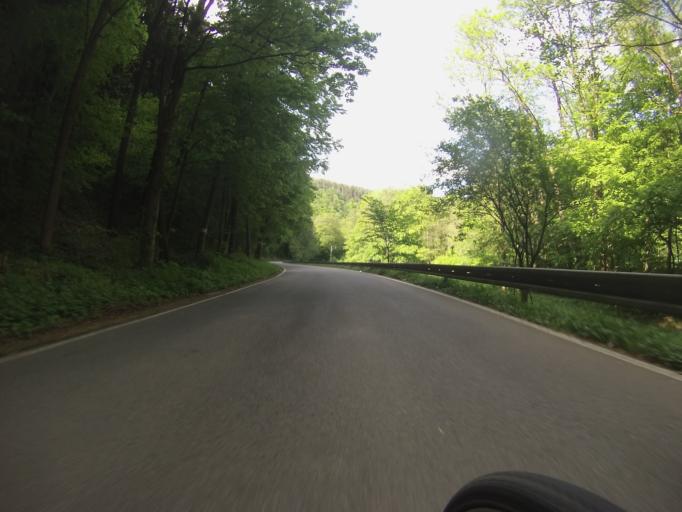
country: CZ
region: South Moravian
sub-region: Okres Blansko
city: Blansko
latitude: 49.3598
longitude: 16.6967
